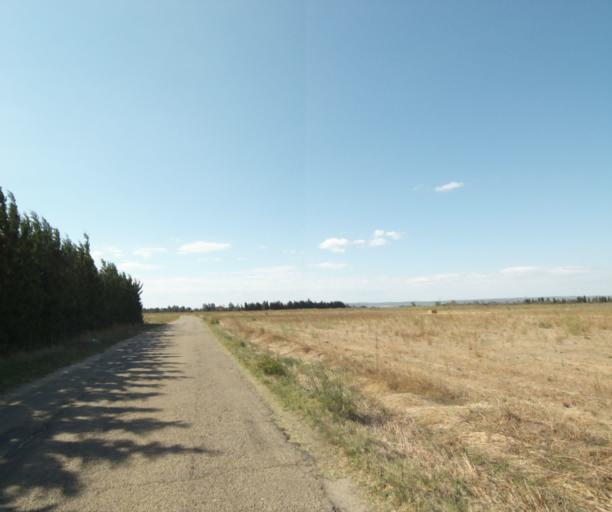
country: FR
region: Languedoc-Roussillon
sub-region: Departement du Gard
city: Bouillargues
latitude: 43.7996
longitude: 4.4514
